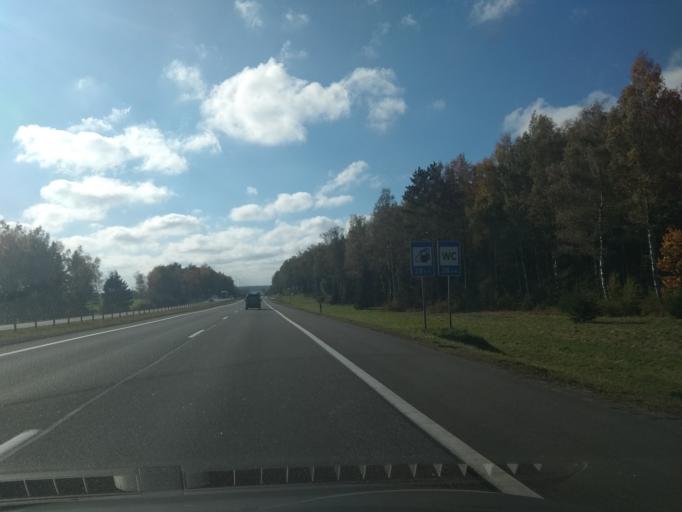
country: BY
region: Minsk
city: Enyerhyetykaw
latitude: 53.6394
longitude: 27.0658
